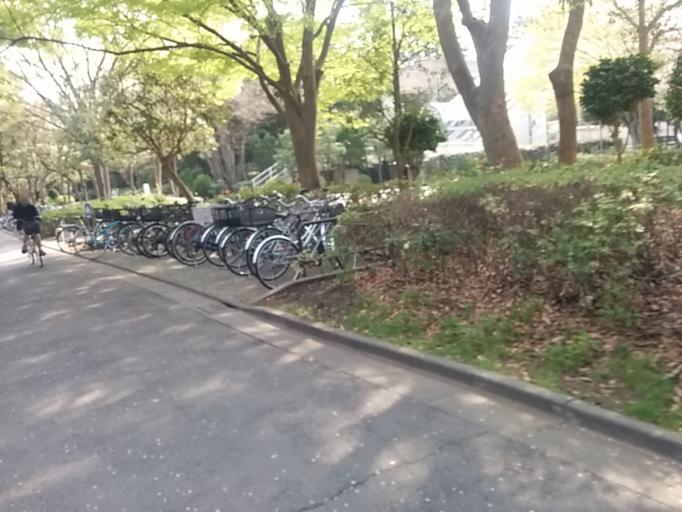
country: JP
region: Tokyo
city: Urayasu
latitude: 35.6506
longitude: 139.8564
